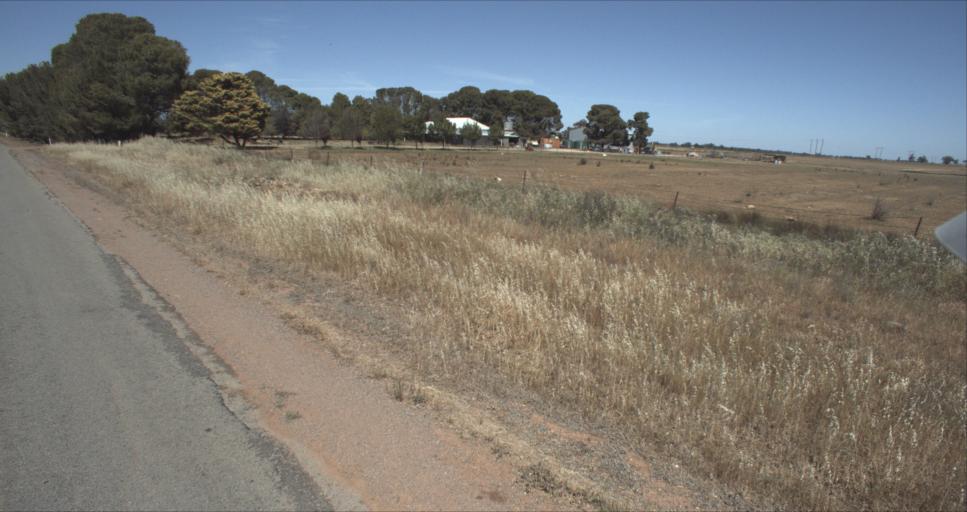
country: AU
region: New South Wales
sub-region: Leeton
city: Leeton
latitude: -34.5712
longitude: 146.3106
